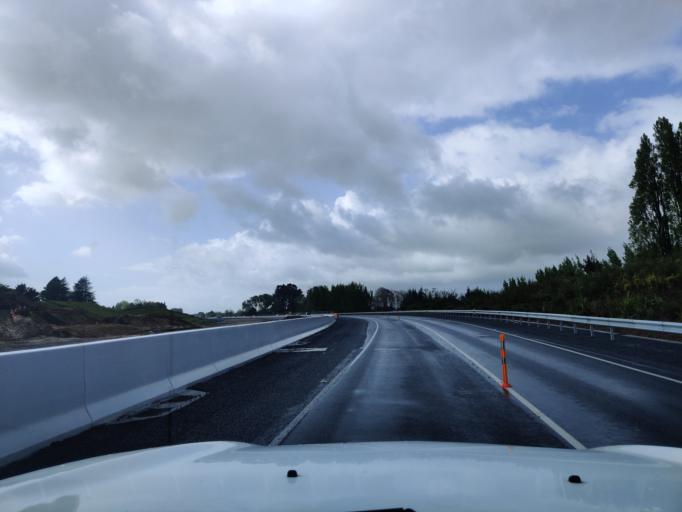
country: NZ
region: Waikato
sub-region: Hamilton City
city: Hamilton
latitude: -37.8167
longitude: 175.3426
